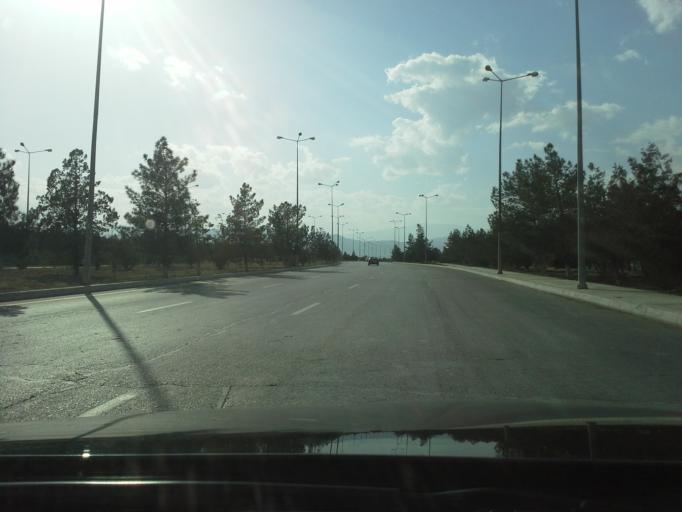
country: TM
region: Ahal
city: Ashgabat
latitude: 37.9710
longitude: 58.2783
